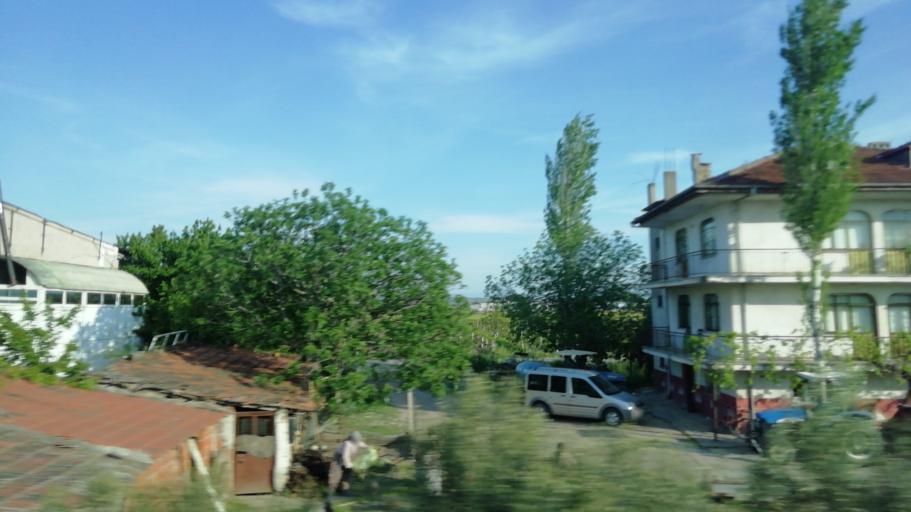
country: TR
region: Manisa
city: Saruhanli
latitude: 38.7307
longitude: 27.5825
